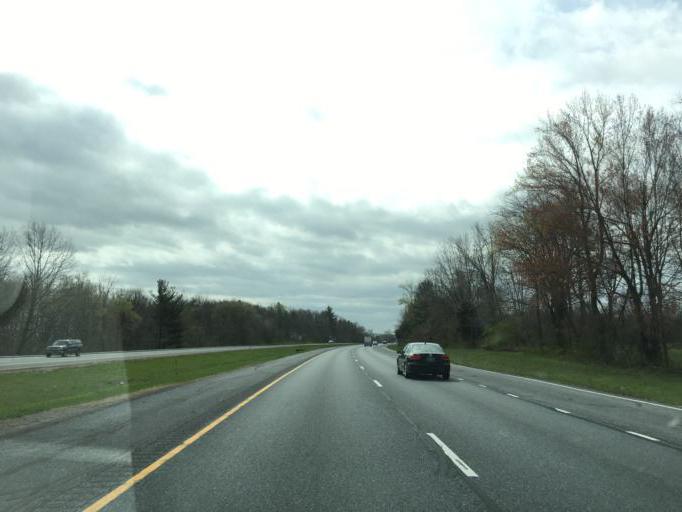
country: US
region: Maryland
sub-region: Frederick County
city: Walkersville
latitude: 39.5019
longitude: -77.4001
